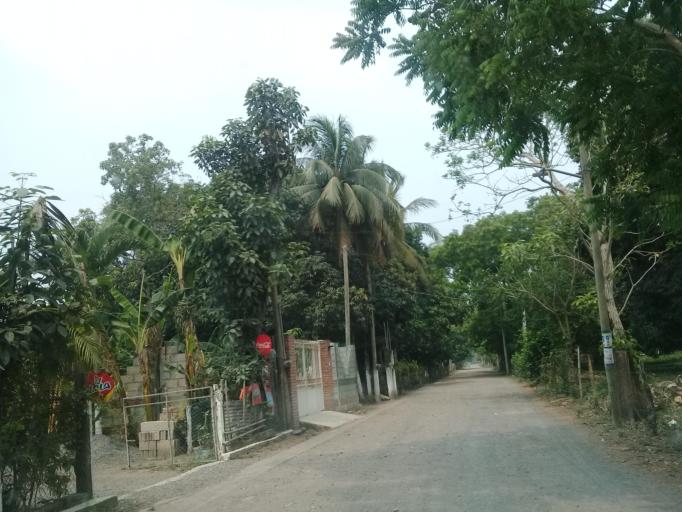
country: MX
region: Veracruz
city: Jamapa
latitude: 18.9520
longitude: -96.1995
